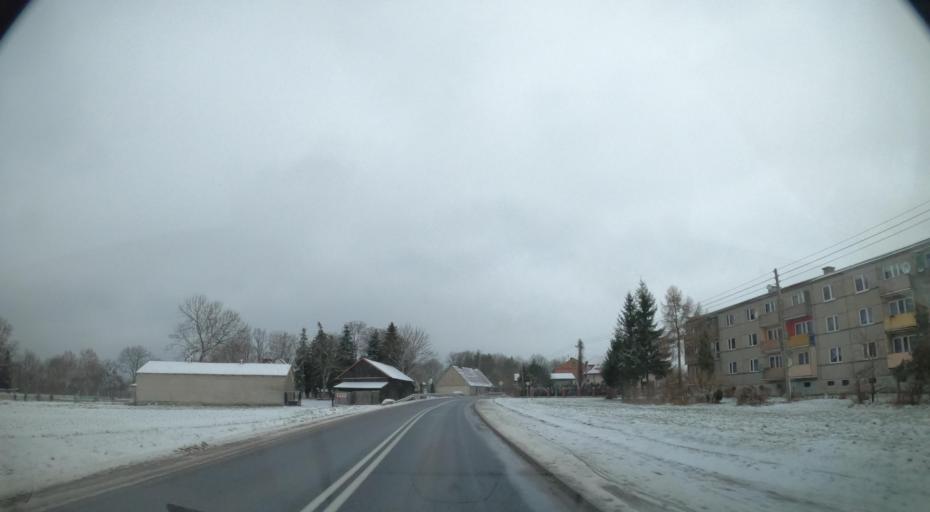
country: PL
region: Masovian Voivodeship
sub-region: Powiat plocki
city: Nowy Duninow
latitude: 52.6136
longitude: 19.4624
